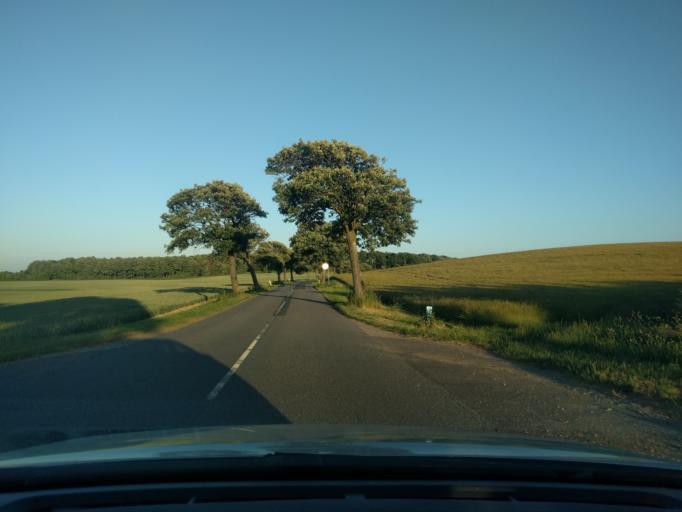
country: DK
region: South Denmark
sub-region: Kerteminde Kommune
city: Kerteminde
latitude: 55.5807
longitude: 10.6401
